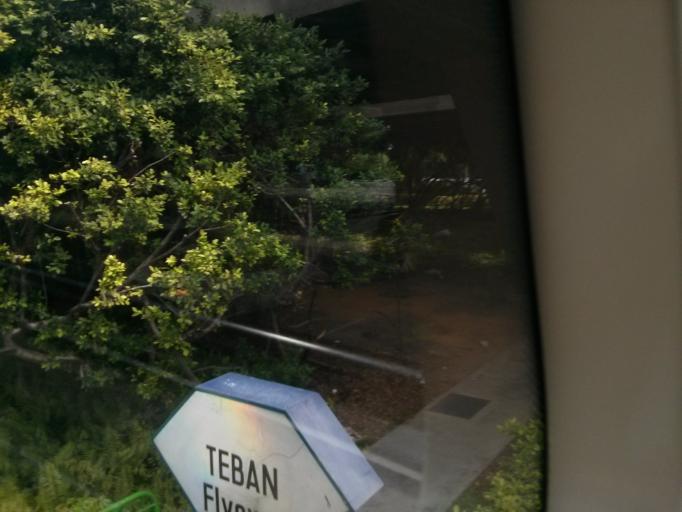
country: SG
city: Singapore
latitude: 1.3231
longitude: 103.7456
